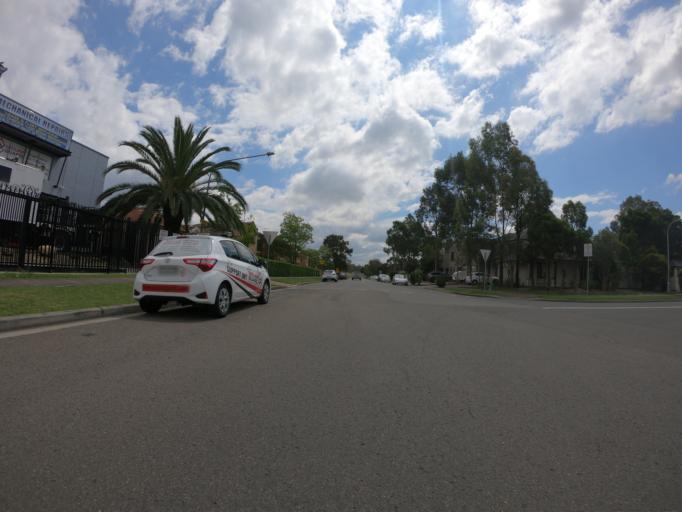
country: AU
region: New South Wales
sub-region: Penrith Municipality
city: Werrington County
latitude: -33.7803
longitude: 150.7695
